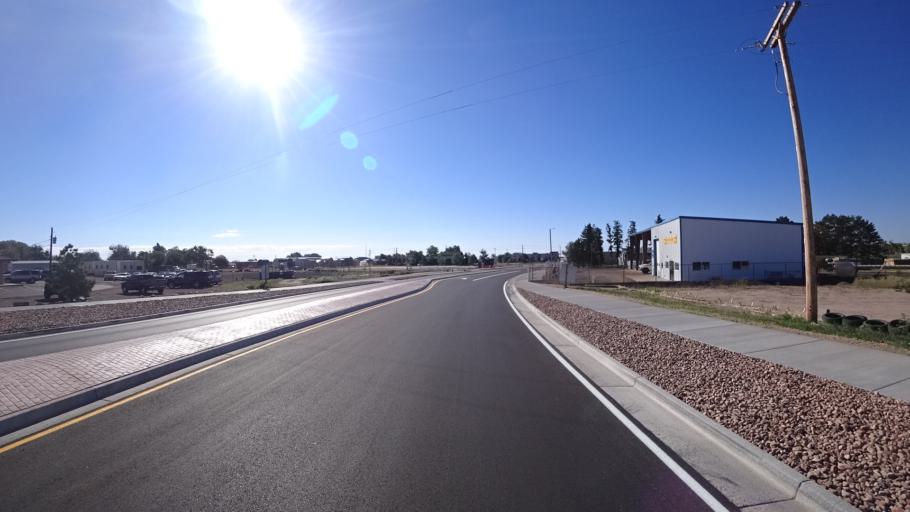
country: US
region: Colorado
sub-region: El Paso County
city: Cimarron Hills
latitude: 38.9349
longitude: -104.6106
